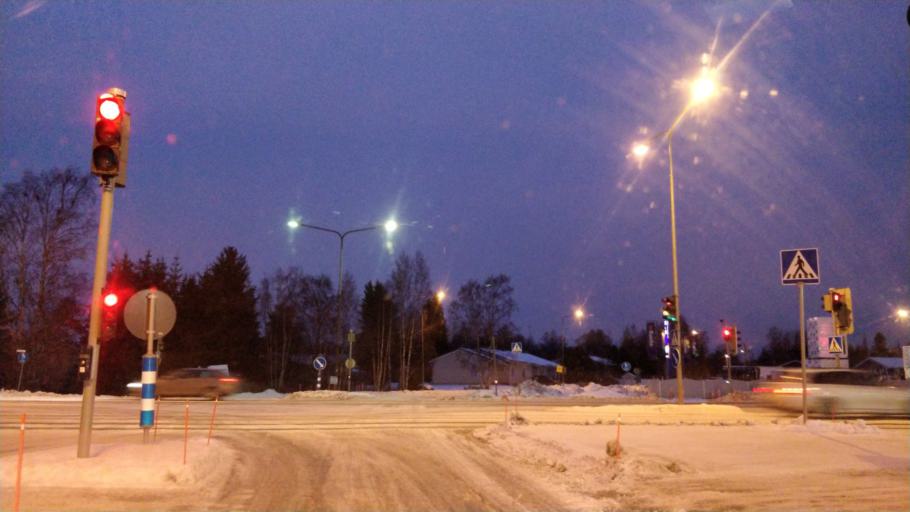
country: FI
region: Lapland
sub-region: Kemi-Tornio
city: Kemi
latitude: 65.7428
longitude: 24.5762
